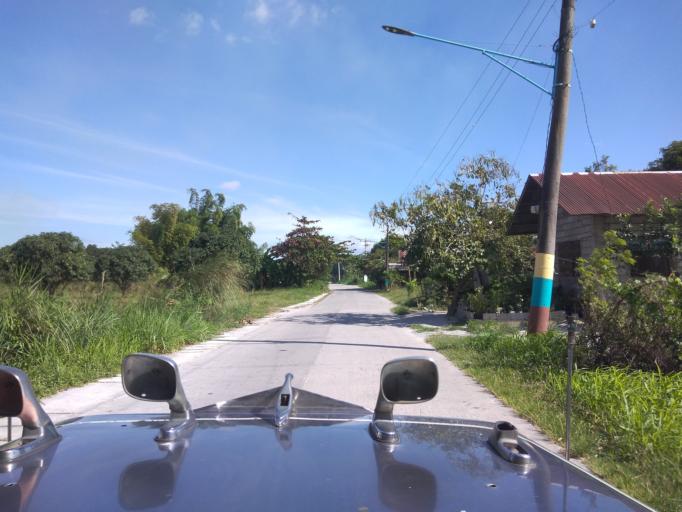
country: PH
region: Central Luzon
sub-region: Province of Pampanga
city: Magliman
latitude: 15.0294
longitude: 120.6304
